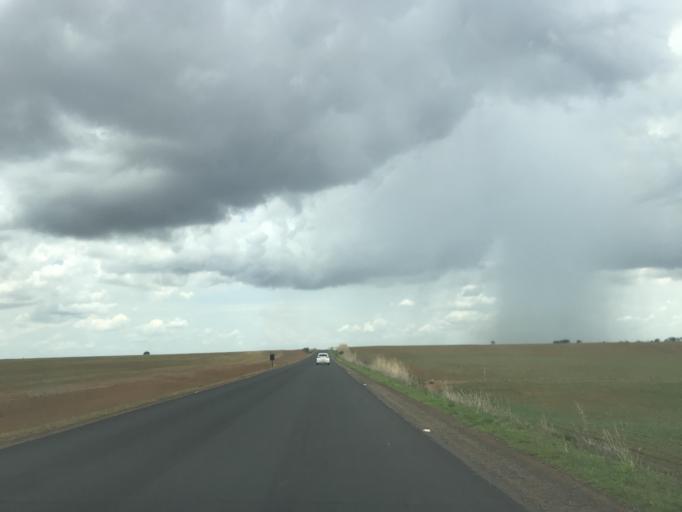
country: BR
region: Goias
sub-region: Vianopolis
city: Vianopolis
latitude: -16.8503
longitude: -48.5376
